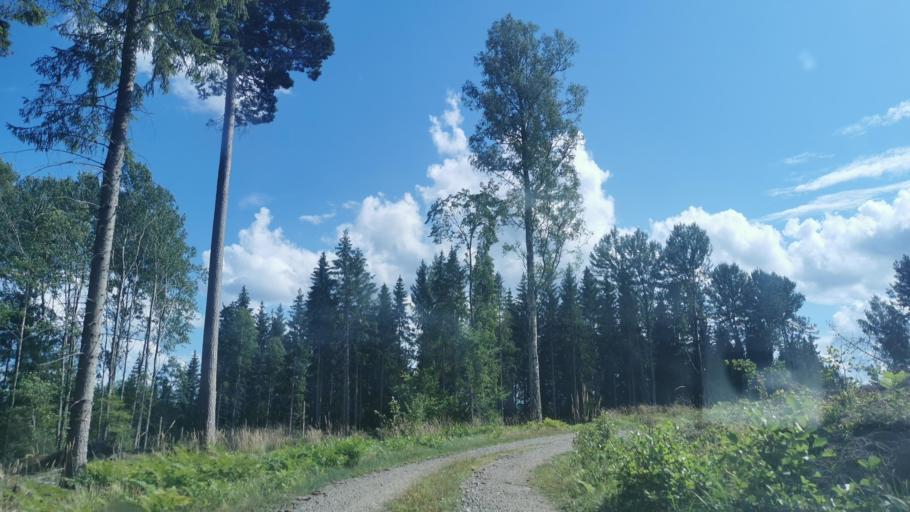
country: SE
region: OEstergoetland
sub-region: Finspangs Kommun
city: Finspang
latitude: 58.7994
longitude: 15.8048
